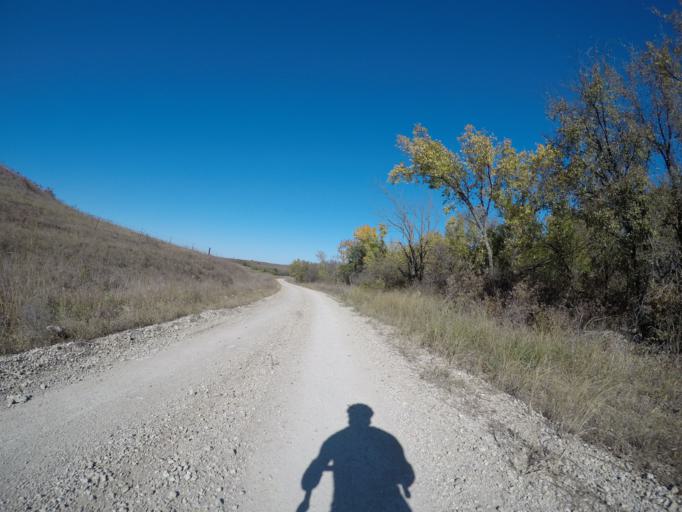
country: US
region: Kansas
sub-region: Wabaunsee County
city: Alma
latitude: 38.9235
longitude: -96.3921
